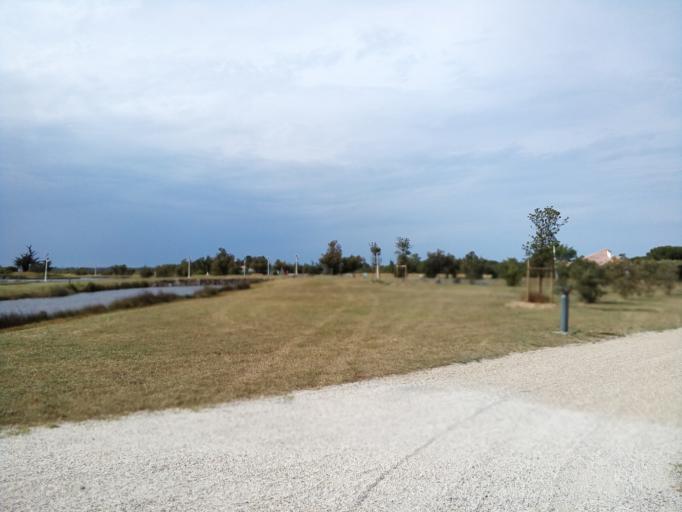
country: FR
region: Poitou-Charentes
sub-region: Departement de la Charente-Maritime
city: Boyard-Ville
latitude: 45.9511
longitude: -1.2464
